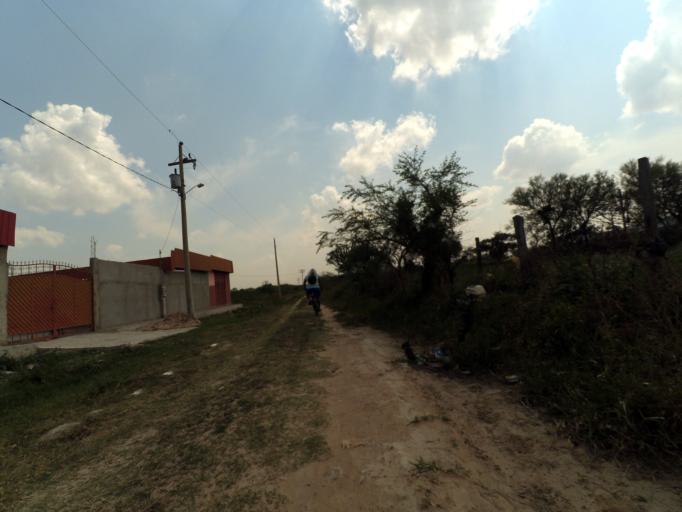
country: BO
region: Santa Cruz
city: Santa Cruz de la Sierra
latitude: -17.8850
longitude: -63.2042
